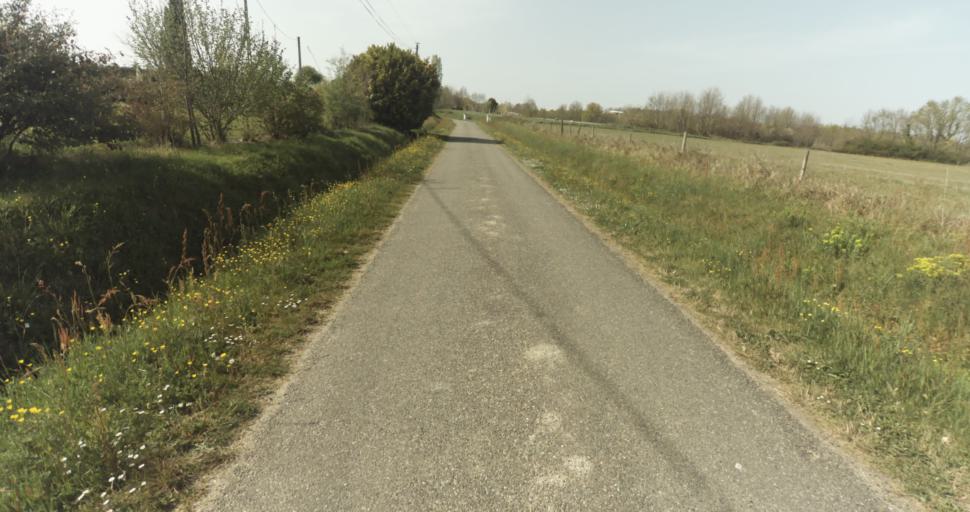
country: FR
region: Midi-Pyrenees
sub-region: Departement du Tarn-et-Garonne
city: Lafrancaise
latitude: 44.1432
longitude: 1.1733
